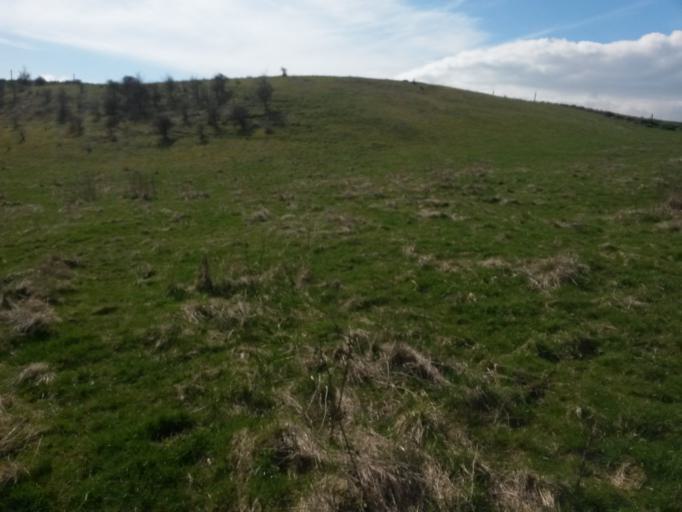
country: SE
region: Skane
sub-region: Kavlinge Kommun
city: Kaevlinge
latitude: 55.7785
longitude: 13.1616
